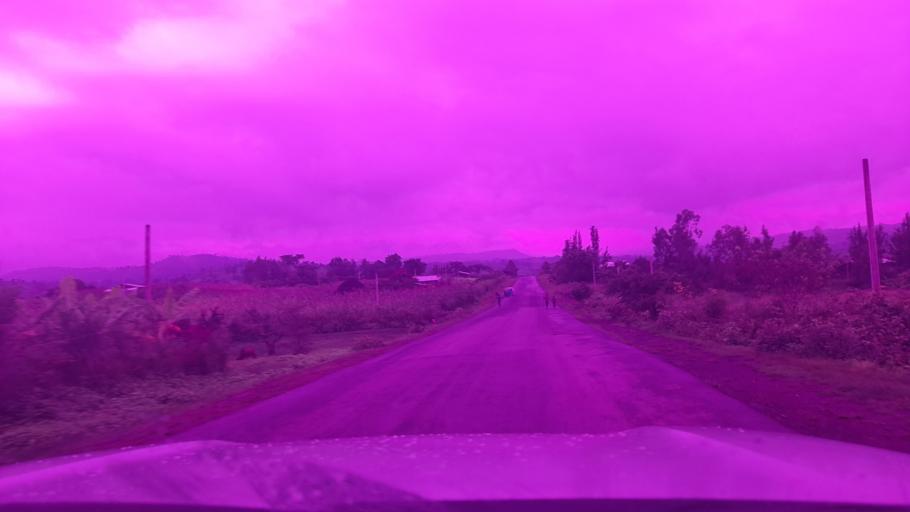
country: ET
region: Oromiya
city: Jima
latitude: 7.7923
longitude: 37.3411
